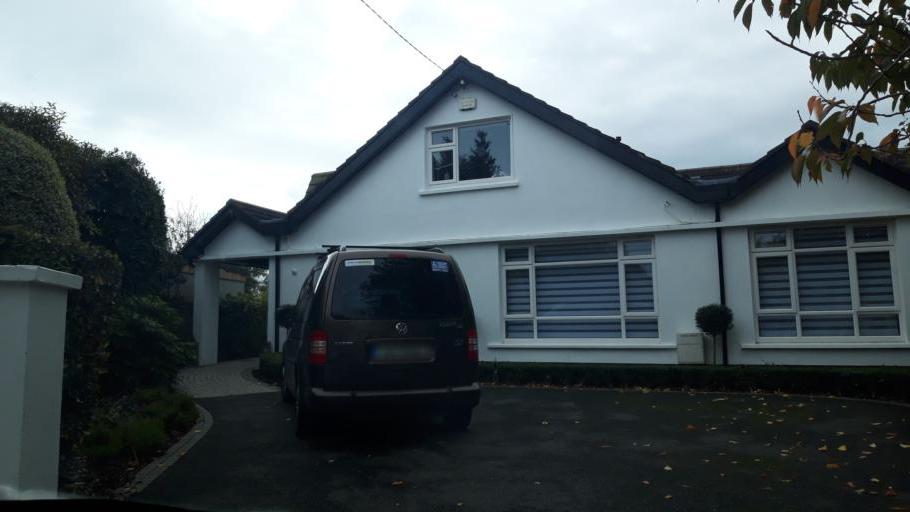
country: IE
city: Milltown
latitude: 53.3089
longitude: -6.2383
